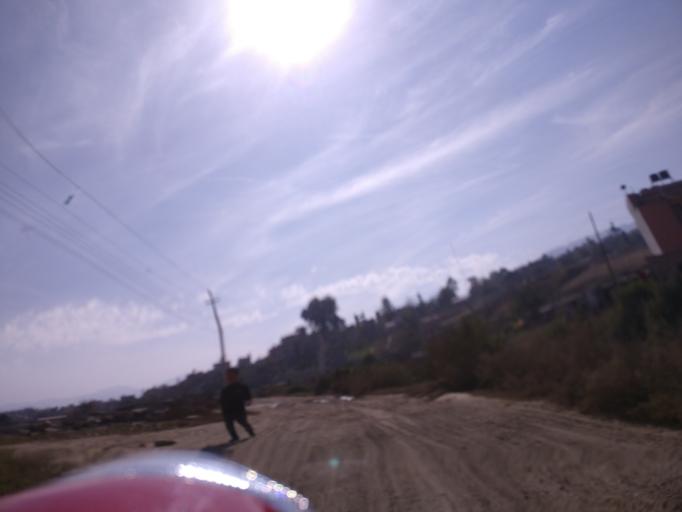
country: NP
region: Central Region
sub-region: Bagmati Zone
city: Patan
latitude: 27.6534
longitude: 85.3126
